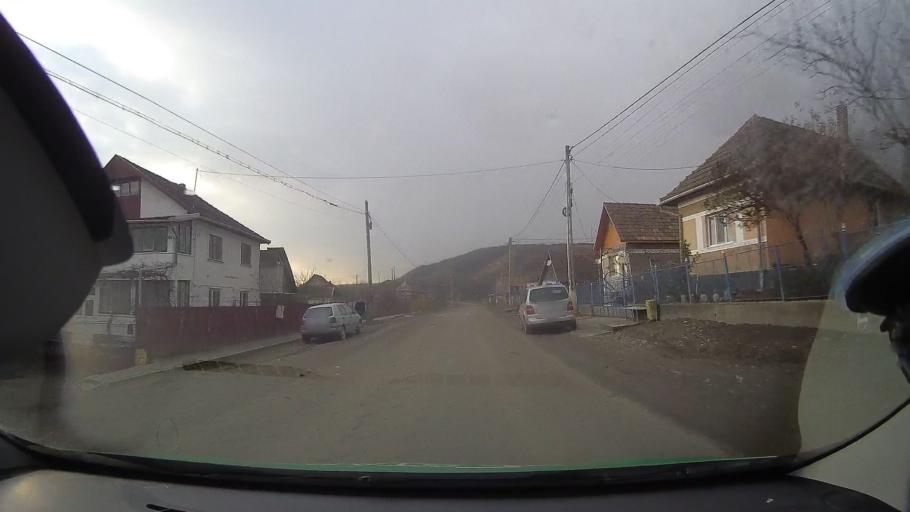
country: RO
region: Alba
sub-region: Comuna Lunca Muresului
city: Lunca Muresului
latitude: 46.4287
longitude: 23.9035
